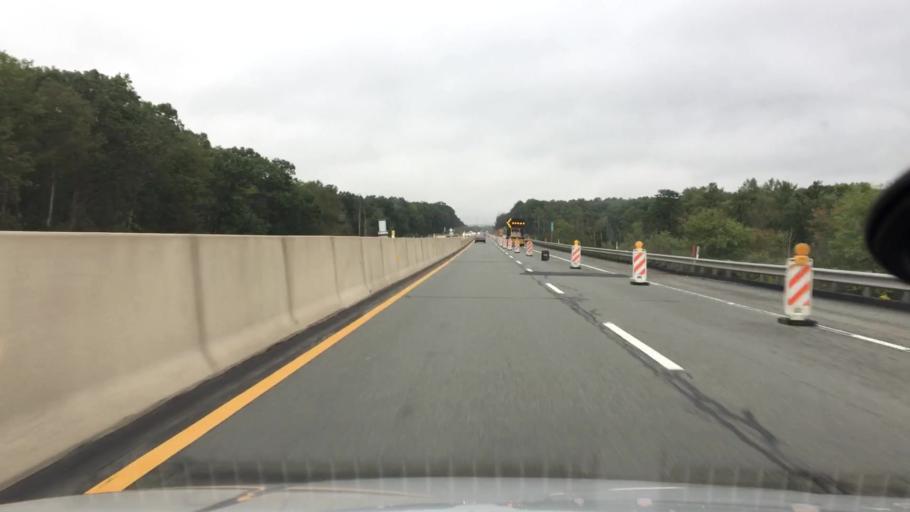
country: US
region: Pennsylvania
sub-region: Luzerne County
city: White Haven
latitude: 41.1130
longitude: -75.7589
